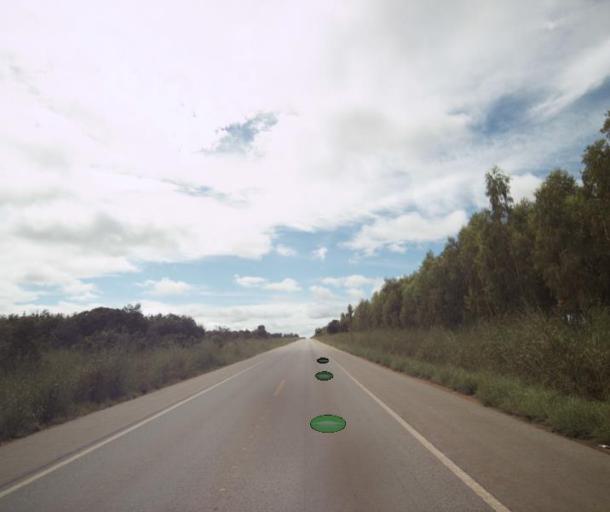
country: BR
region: Goias
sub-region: Barro Alto
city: Barro Alto
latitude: -15.2055
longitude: -48.7260
